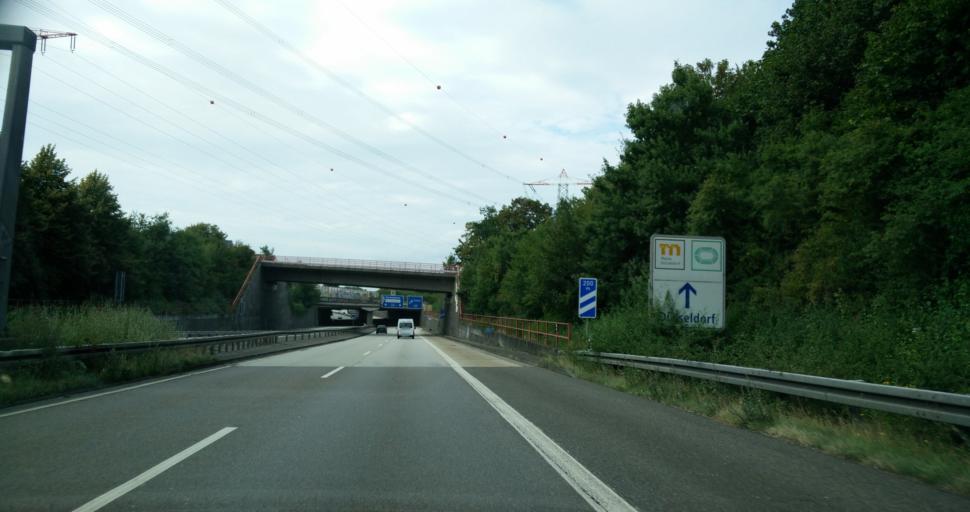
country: DE
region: North Rhine-Westphalia
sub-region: Regierungsbezirk Dusseldorf
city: Ratingen
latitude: 51.2840
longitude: 6.8060
